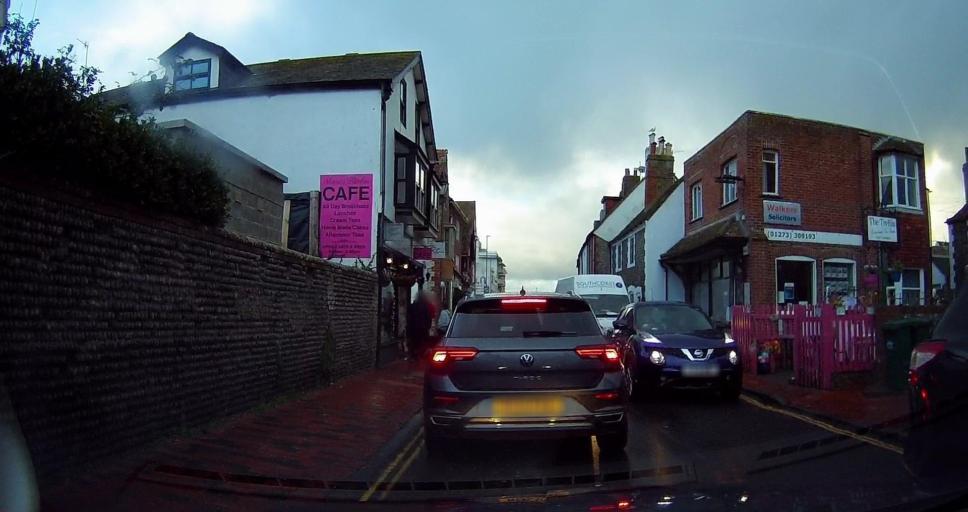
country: GB
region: England
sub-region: Brighton and Hove
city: Rottingdean
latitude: 50.8042
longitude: -0.0577
